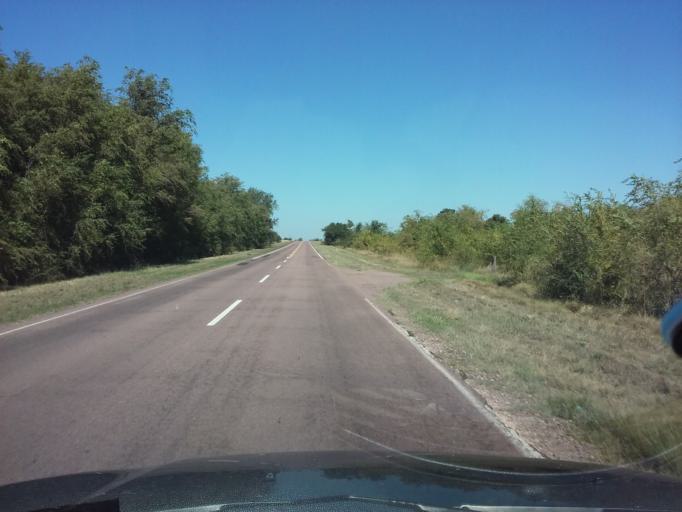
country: AR
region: La Pampa
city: Uriburu
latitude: -36.3794
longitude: -63.9431
